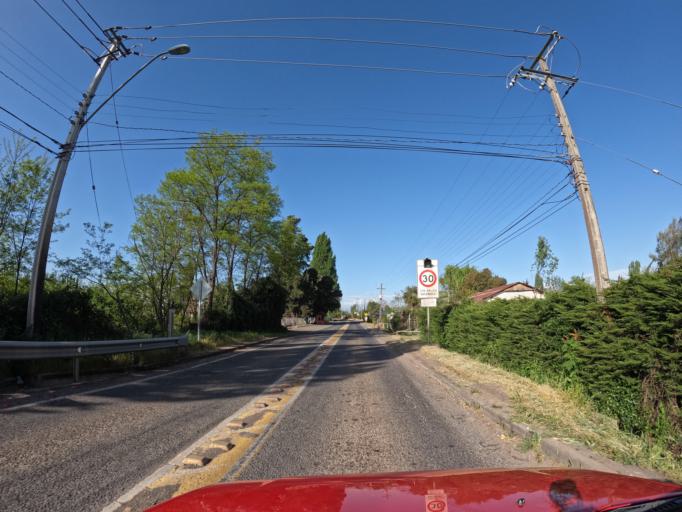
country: CL
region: Maule
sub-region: Provincia de Curico
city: Teno
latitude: -34.8627
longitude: -71.1984
